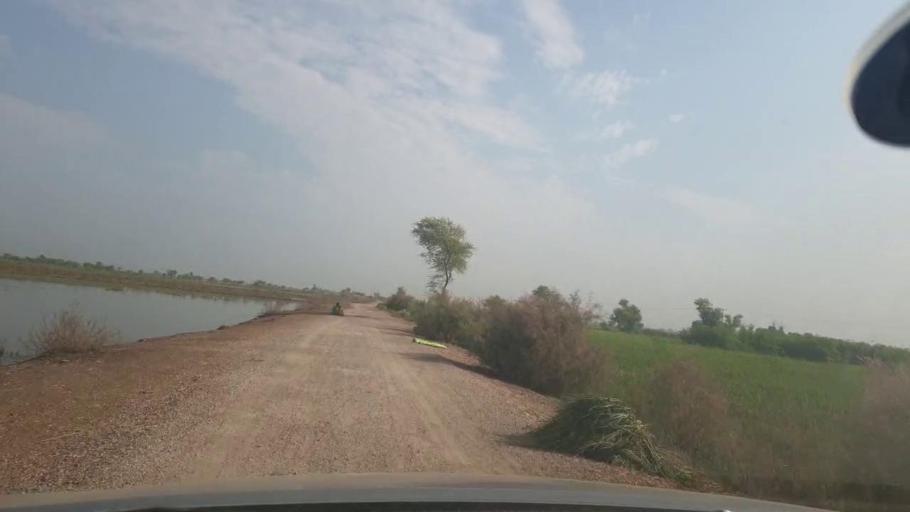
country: PK
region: Balochistan
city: Mehrabpur
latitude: 28.0659
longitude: 68.2101
